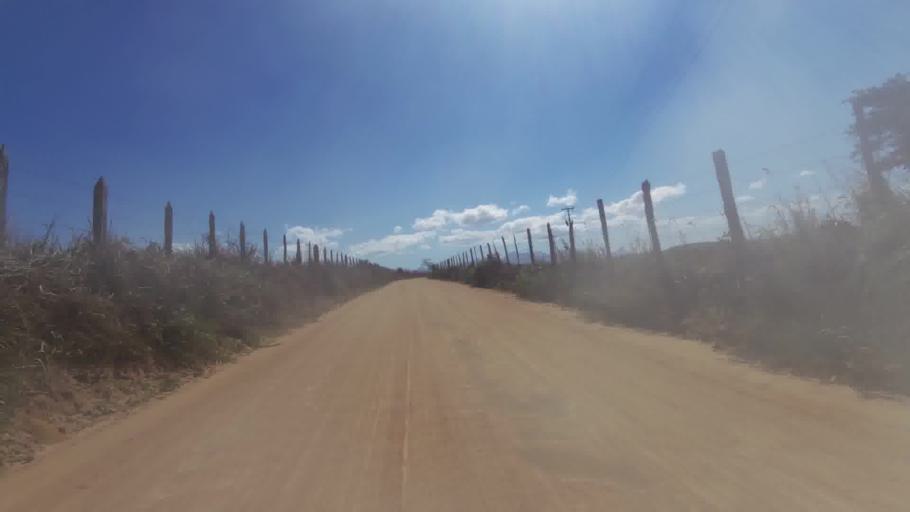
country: BR
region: Espirito Santo
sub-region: Marataizes
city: Marataizes
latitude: -21.1567
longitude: -40.9797
